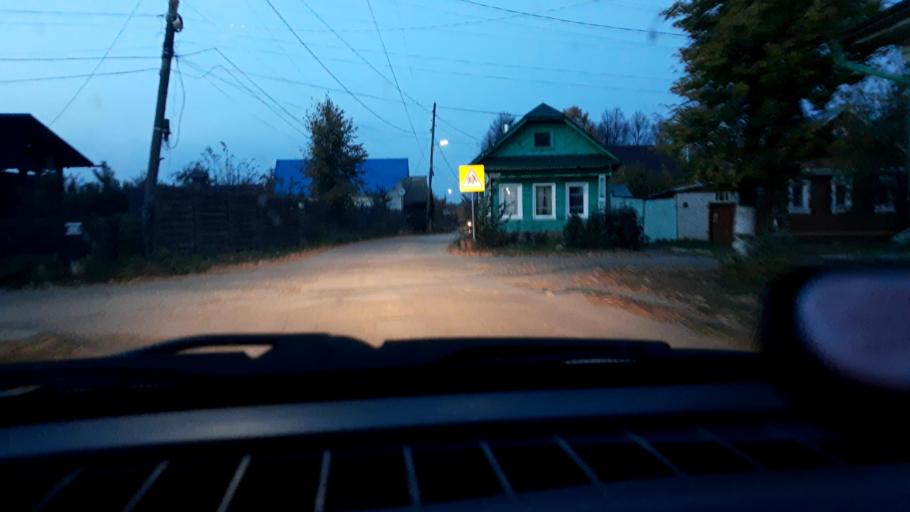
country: RU
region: Nizjnij Novgorod
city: Gorodets
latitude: 56.6361
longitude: 43.4692
